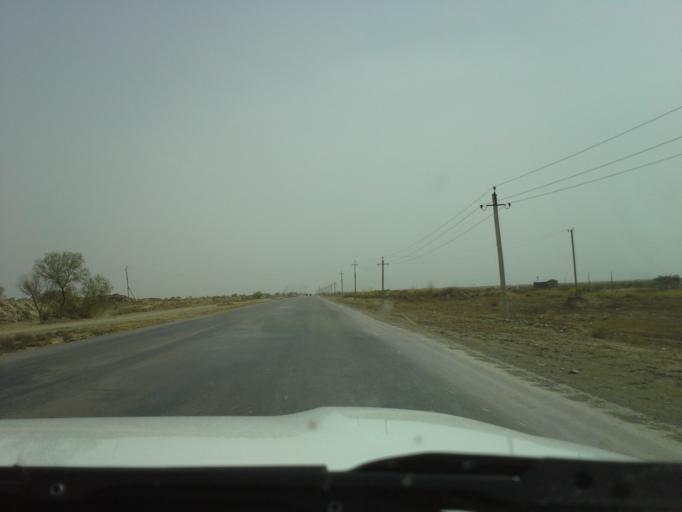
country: TM
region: Ahal
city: Tejen
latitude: 37.2258
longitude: 61.1306
